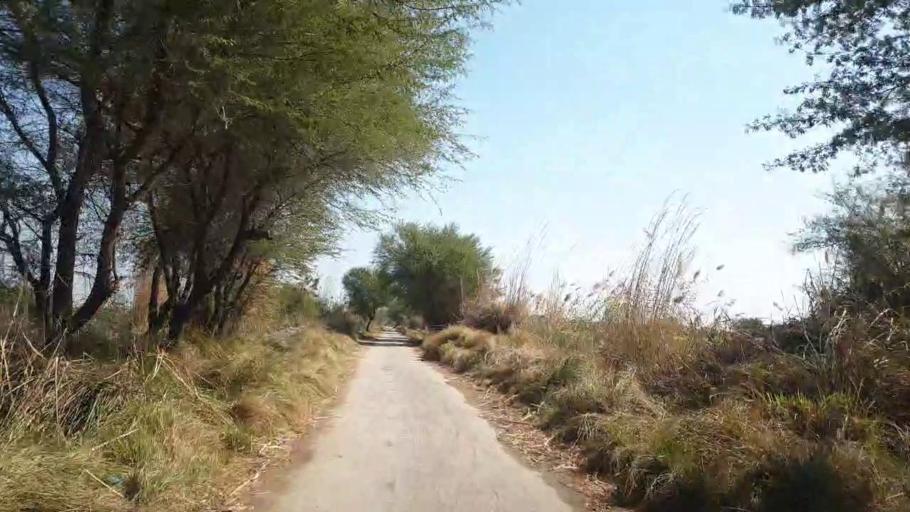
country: PK
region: Sindh
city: Mirpur Khas
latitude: 25.6442
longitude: 69.0260
